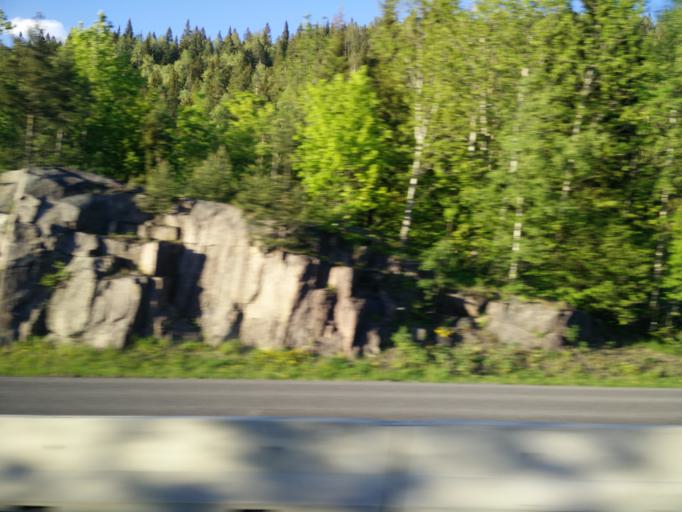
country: NO
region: Buskerud
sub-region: Hole
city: Vik
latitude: 59.9829
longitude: 10.3095
